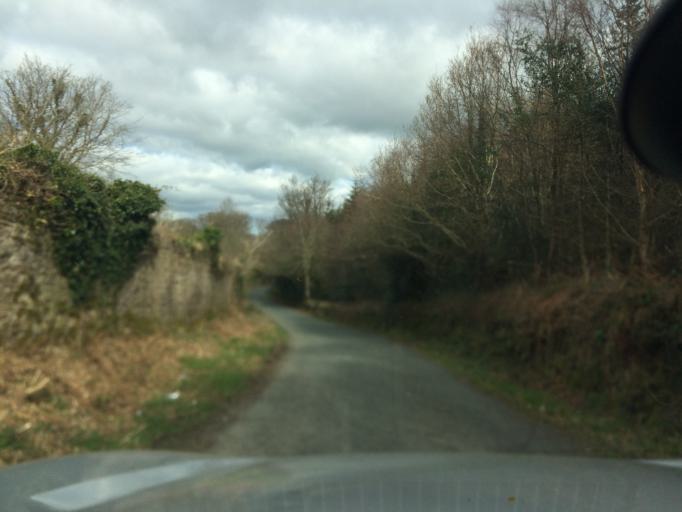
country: IE
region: Munster
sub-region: Waterford
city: Portlaw
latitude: 52.2855
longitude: -7.3372
